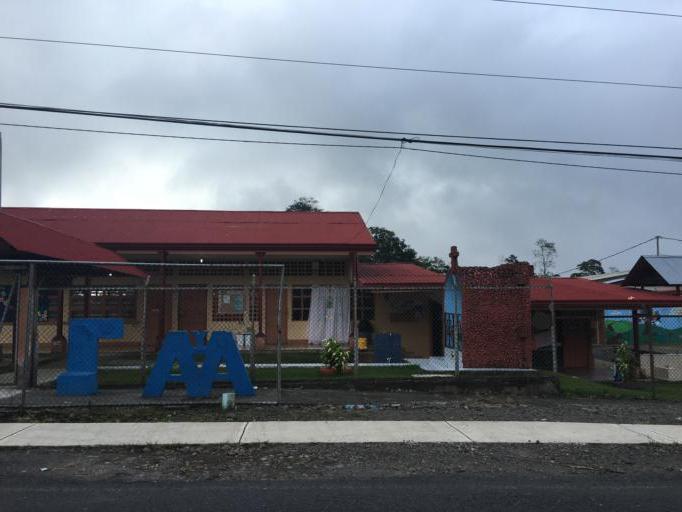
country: CR
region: Cartago
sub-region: Canton de Turrialba
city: La Suiza
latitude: 9.9169
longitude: -83.6152
